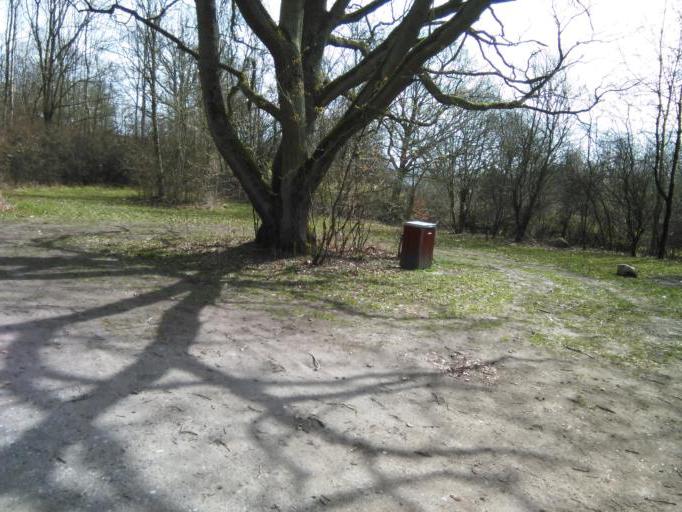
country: DK
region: Central Jutland
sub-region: Arhus Kommune
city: Beder
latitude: 56.0903
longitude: 10.2437
